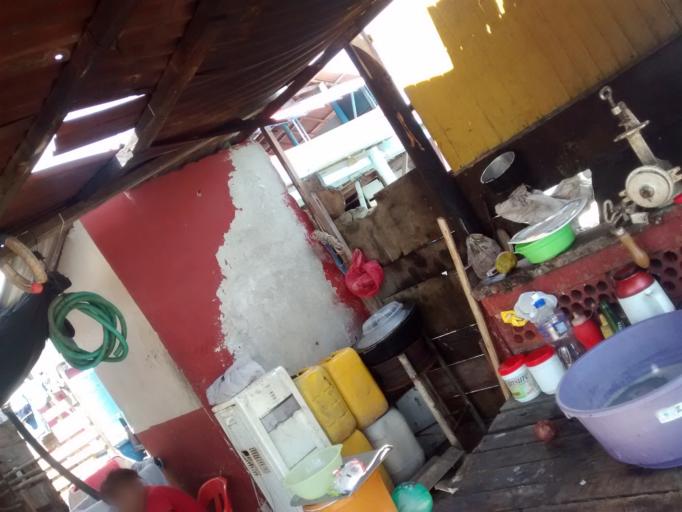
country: CO
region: Sucre
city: San Onofre
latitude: 9.7857
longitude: -75.8596
